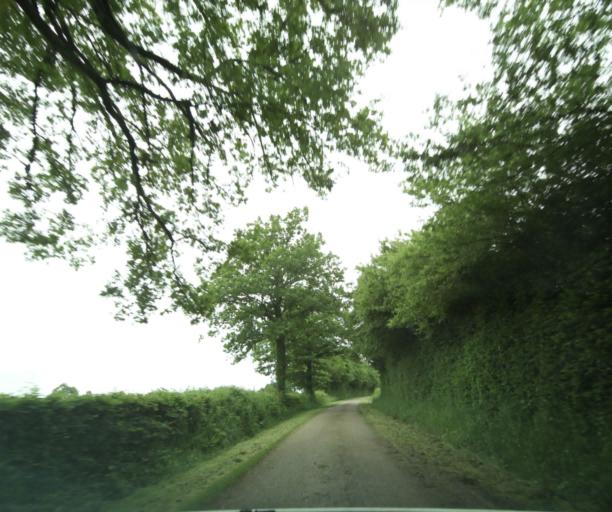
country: FR
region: Bourgogne
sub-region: Departement de Saone-et-Loire
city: Charolles
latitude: 46.4646
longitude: 4.2852
